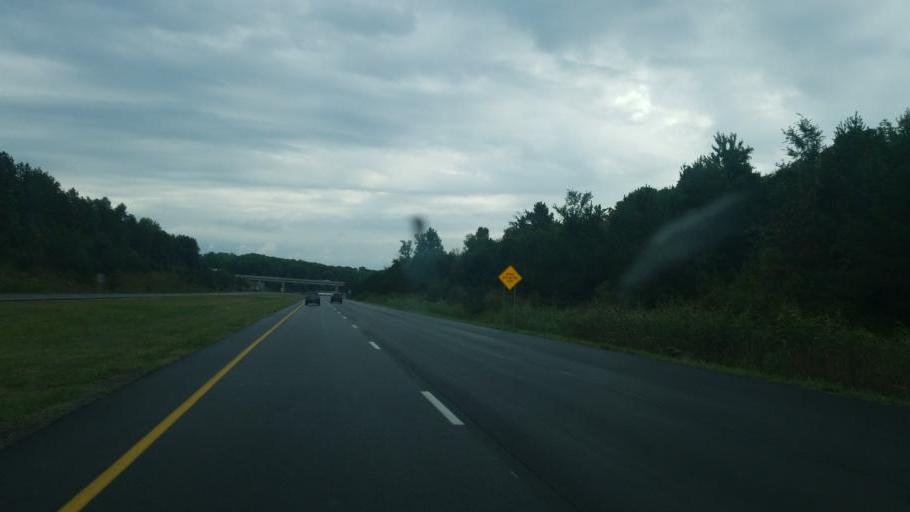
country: US
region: Ohio
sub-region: Summit County
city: Peninsula
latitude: 41.2479
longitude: -81.5887
